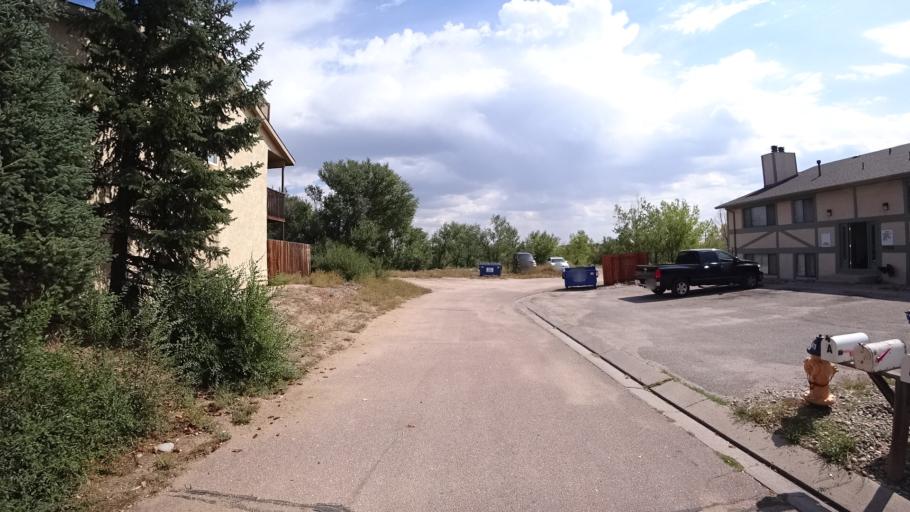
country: US
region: Colorado
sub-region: El Paso County
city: Cimarron Hills
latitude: 38.8581
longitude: -104.7246
